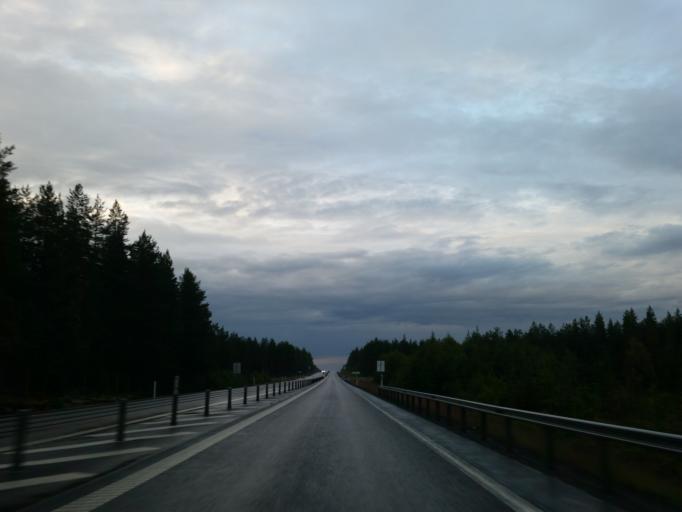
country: SE
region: Vaesterbotten
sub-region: Umea Kommun
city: Saevar
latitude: 63.9338
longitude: 20.6426
